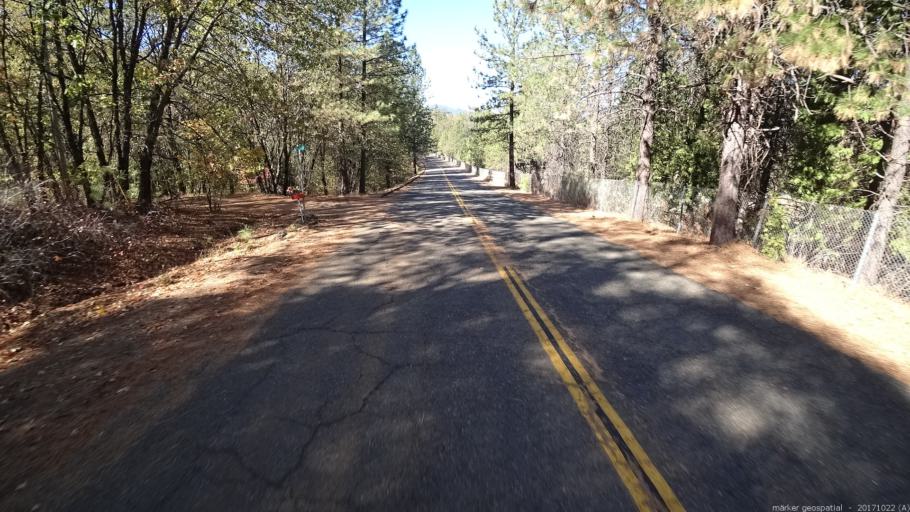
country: US
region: California
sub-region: Shasta County
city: Central Valley (historical)
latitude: 40.9148
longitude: -122.3933
